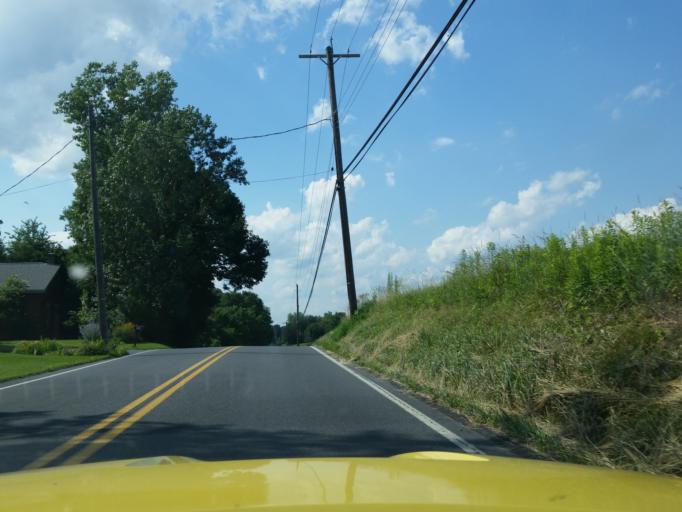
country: US
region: Pennsylvania
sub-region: Lebanon County
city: Annville
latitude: 40.2795
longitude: -76.4868
